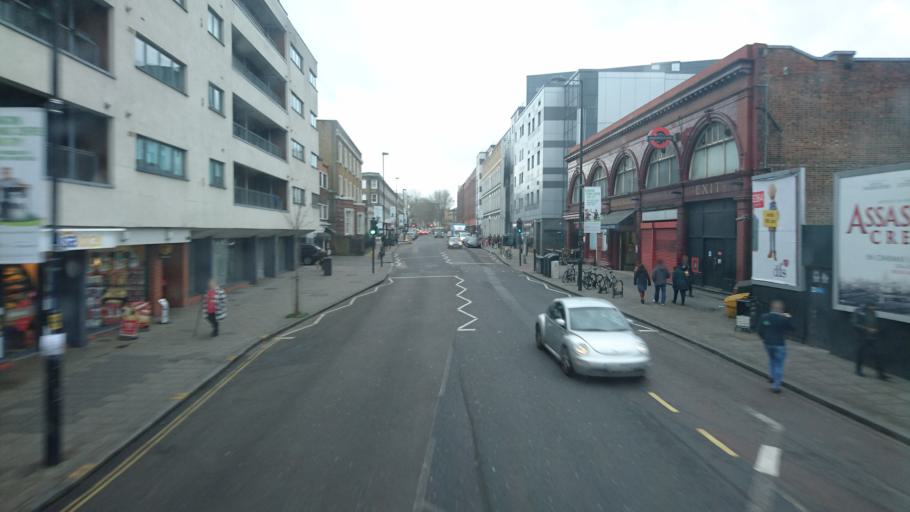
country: GB
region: England
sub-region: Greater London
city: Holloway
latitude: 51.5488
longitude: -0.1180
